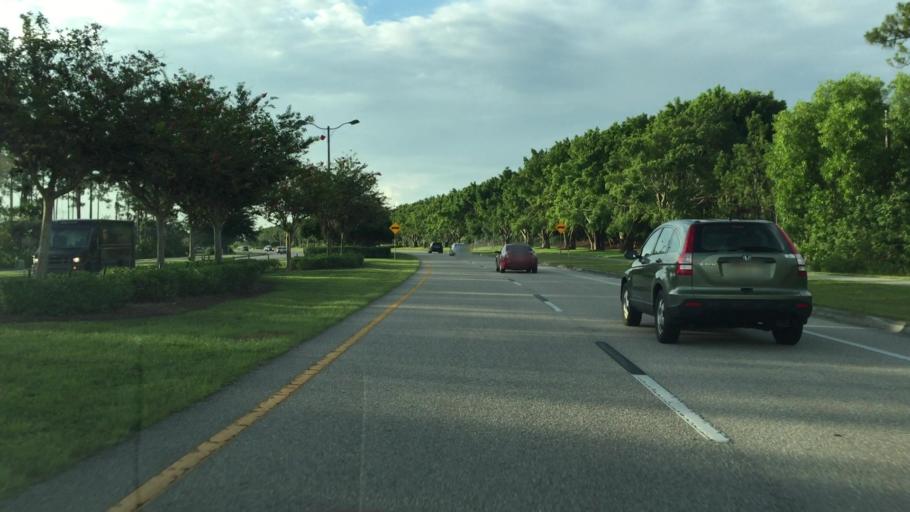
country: US
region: Florida
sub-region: Lee County
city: Three Oaks
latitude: 26.4585
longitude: -81.7826
